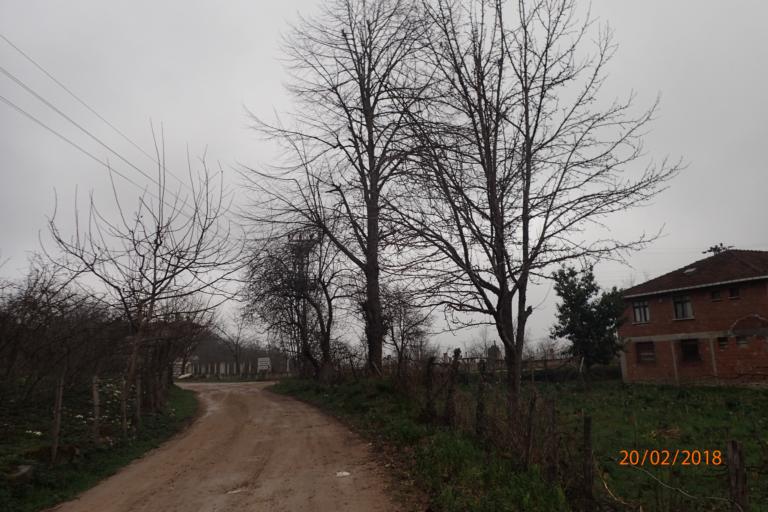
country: TR
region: Ordu
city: Camas
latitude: 40.9476
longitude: 37.5219
